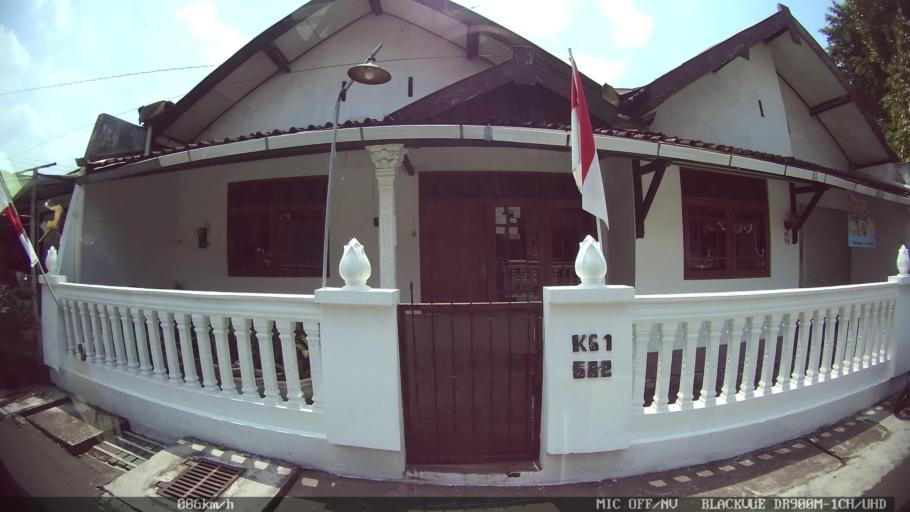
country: ID
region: Daerah Istimewa Yogyakarta
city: Yogyakarta
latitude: -7.8147
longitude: 110.3952
